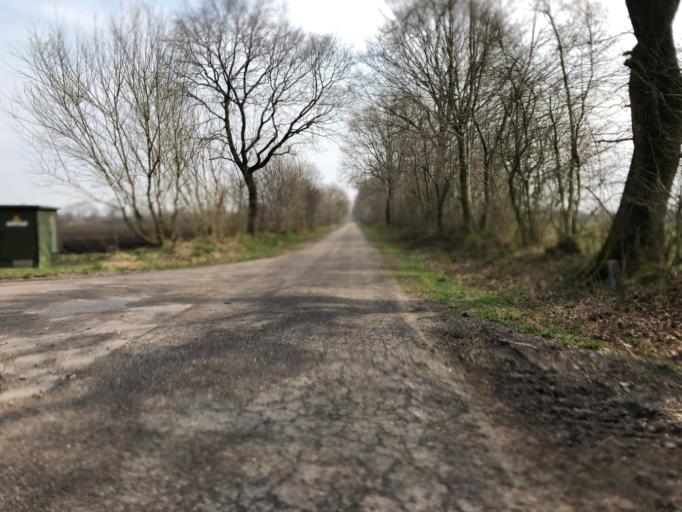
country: DE
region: Schleswig-Holstein
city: Wanderup
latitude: 54.6888
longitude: 9.3152
